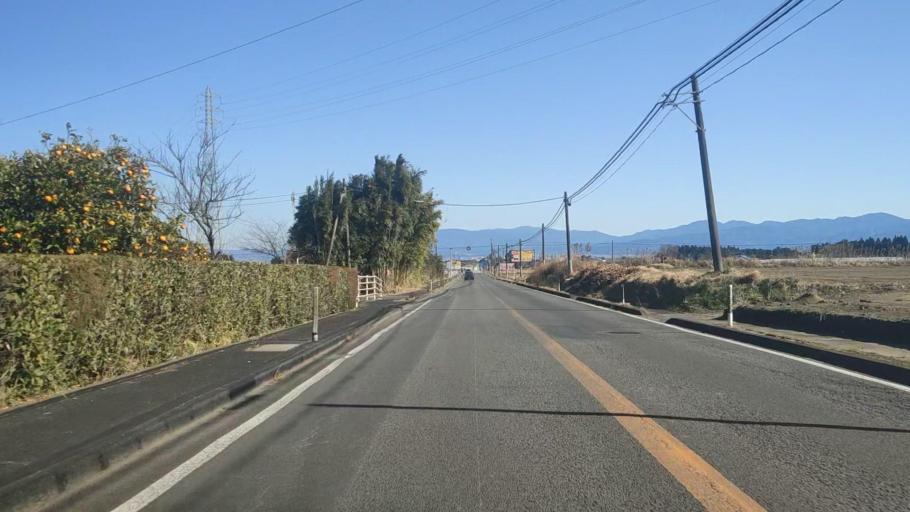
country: JP
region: Kagoshima
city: Sueyoshicho-ninokata
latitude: 31.6960
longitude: 130.9990
